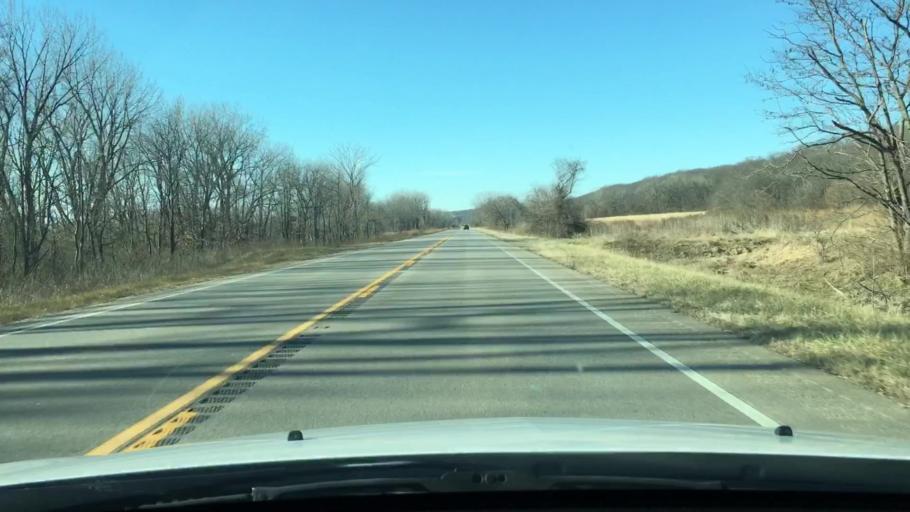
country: US
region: Illinois
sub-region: Peoria County
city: Glasford
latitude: 40.5508
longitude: -89.8150
